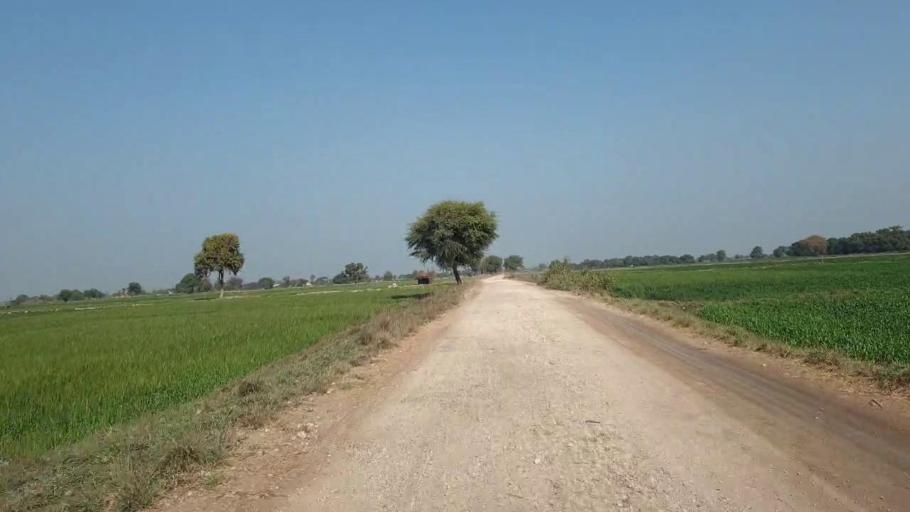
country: PK
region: Sindh
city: Hala
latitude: 25.9121
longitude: 68.4197
